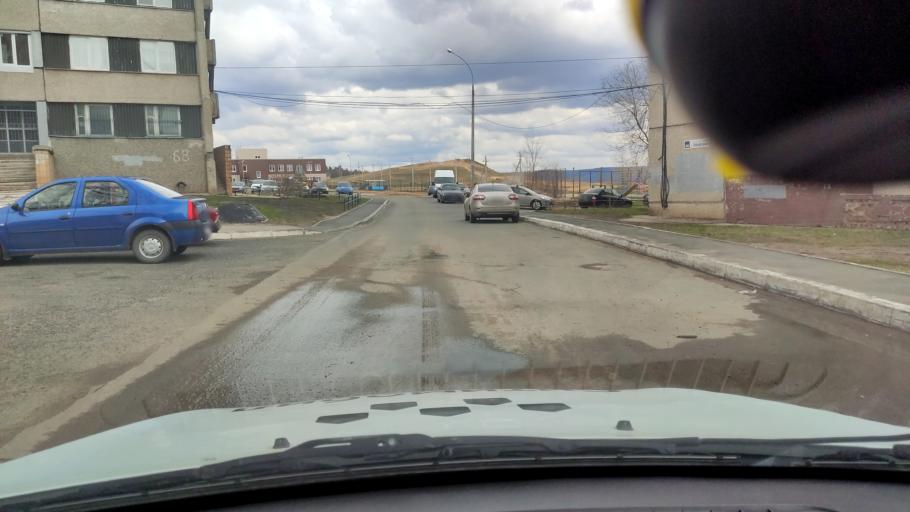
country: RU
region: Samara
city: Zhigulevsk
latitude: 53.4802
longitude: 49.5263
